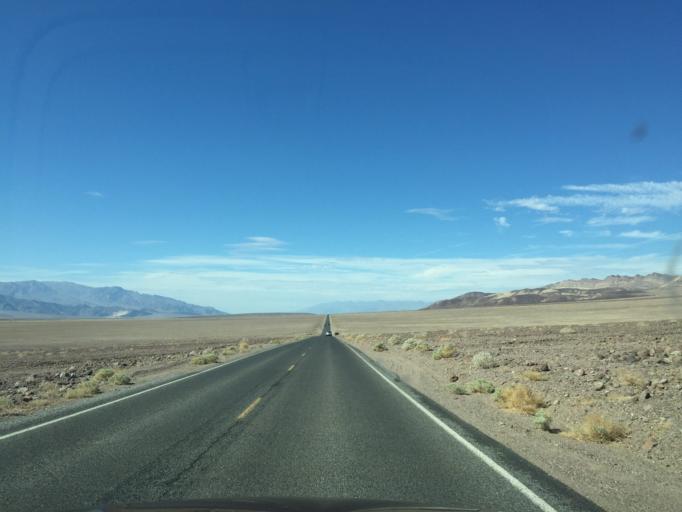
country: US
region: Nevada
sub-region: Nye County
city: Beatty
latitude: 36.2821
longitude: -116.8022
